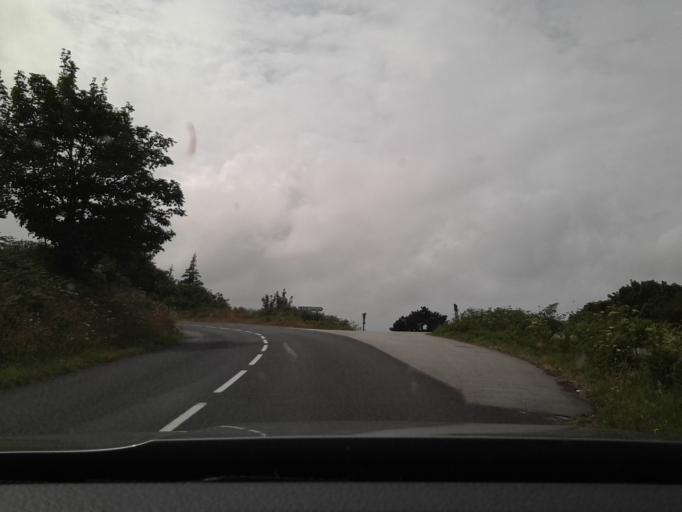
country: FR
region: Lower Normandy
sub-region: Departement de la Manche
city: Urville-Nacqueville
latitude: 49.6794
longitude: -1.7690
